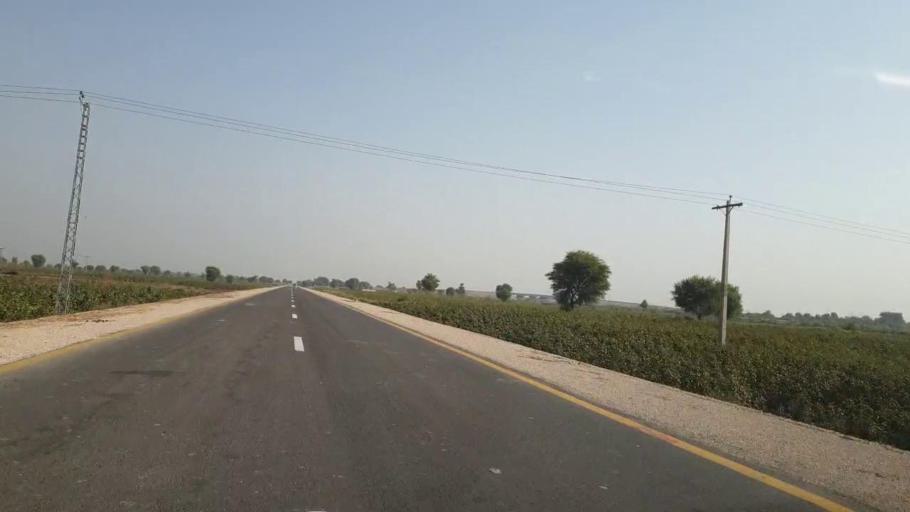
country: PK
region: Sindh
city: Sehwan
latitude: 26.4637
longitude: 67.7996
